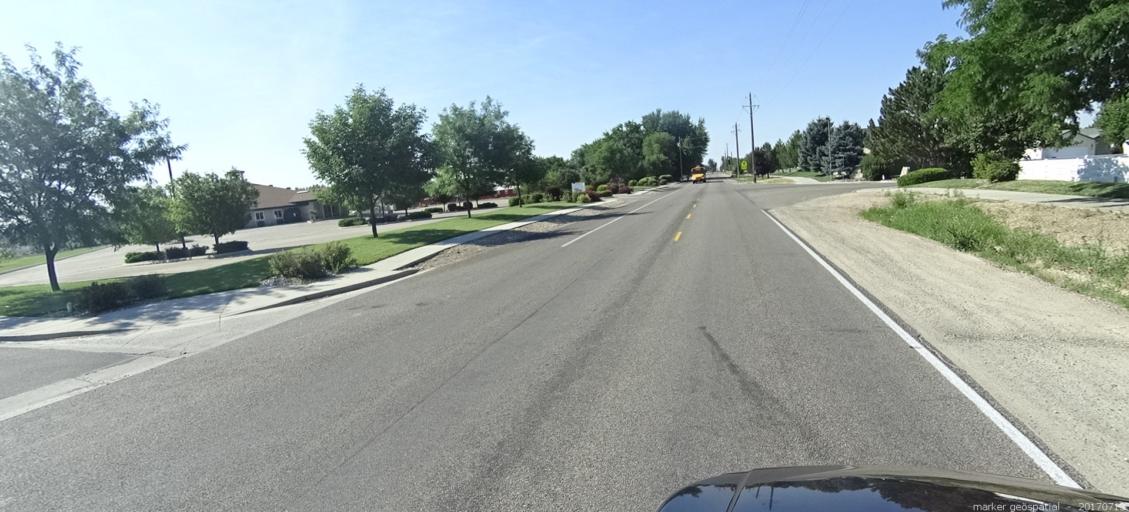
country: US
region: Idaho
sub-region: Ada County
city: Kuna
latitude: 43.5010
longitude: -116.4137
